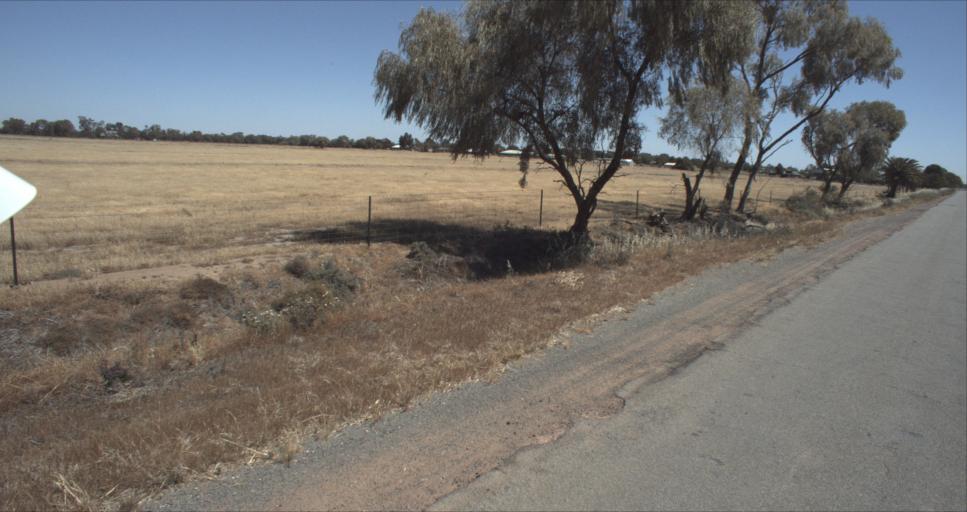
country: AU
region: New South Wales
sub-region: Leeton
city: Leeton
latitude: -34.5447
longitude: 146.4250
